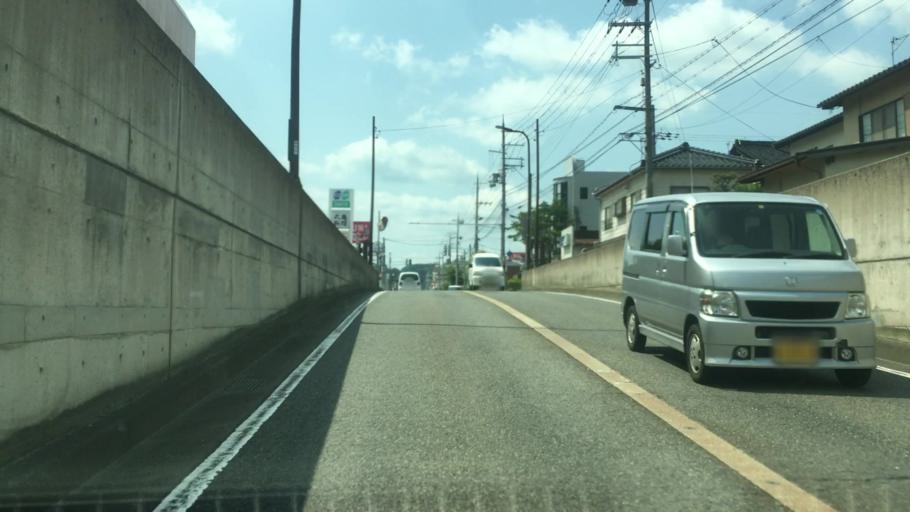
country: JP
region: Hyogo
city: Toyooka
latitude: 35.5510
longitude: 134.8155
